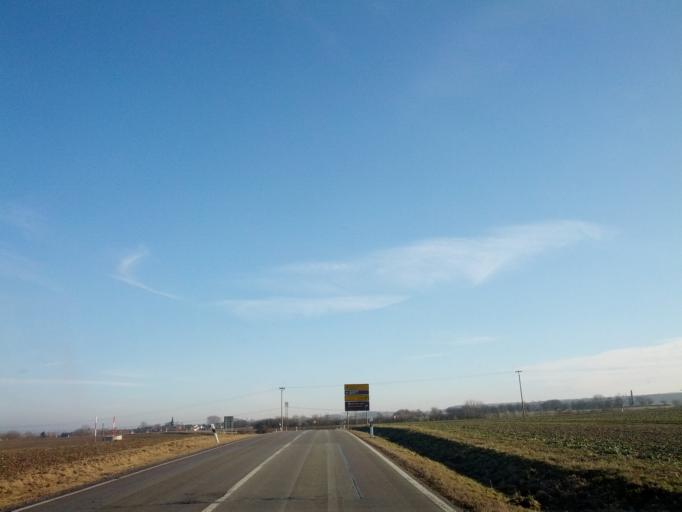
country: DE
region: Thuringia
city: Schonstedt
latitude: 51.0920
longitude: 10.5611
